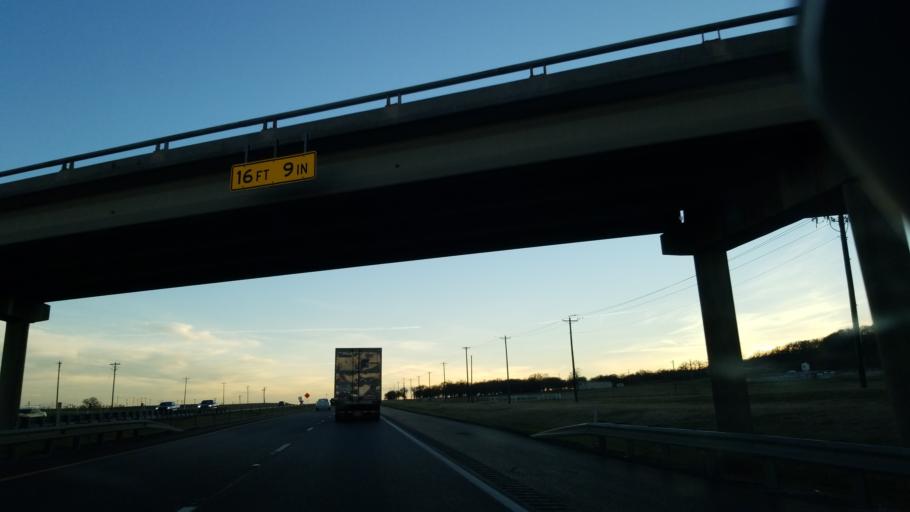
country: US
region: Texas
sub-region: Denton County
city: Argyle
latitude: 33.1542
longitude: -97.1921
